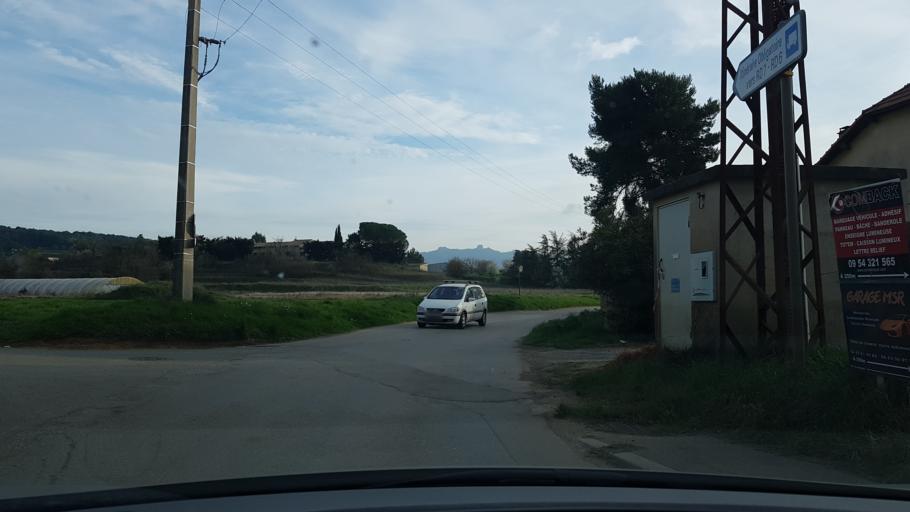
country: FR
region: Provence-Alpes-Cote d'Azur
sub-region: Departement des Bouches-du-Rhone
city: Gardanne
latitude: 43.4706
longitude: 5.4659
